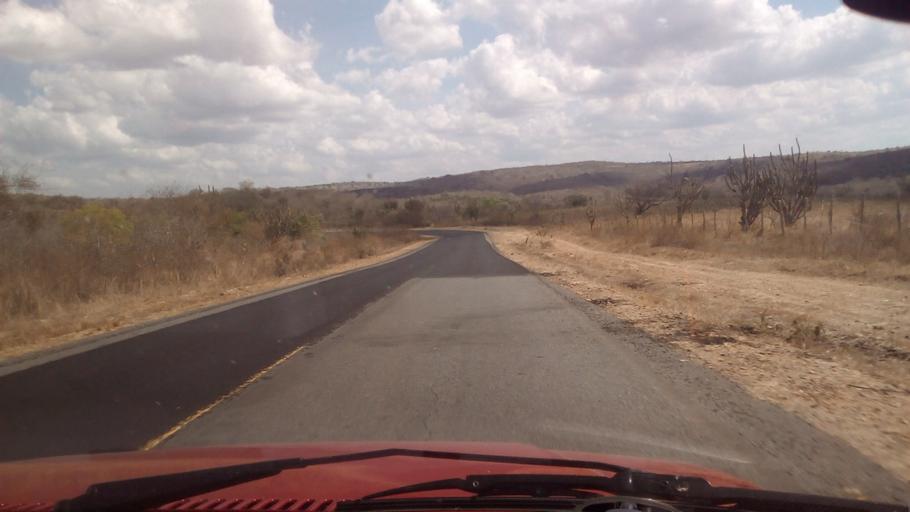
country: BR
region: Paraiba
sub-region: Bananeiras
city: Bananeiras
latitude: -6.7175
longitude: -35.7177
